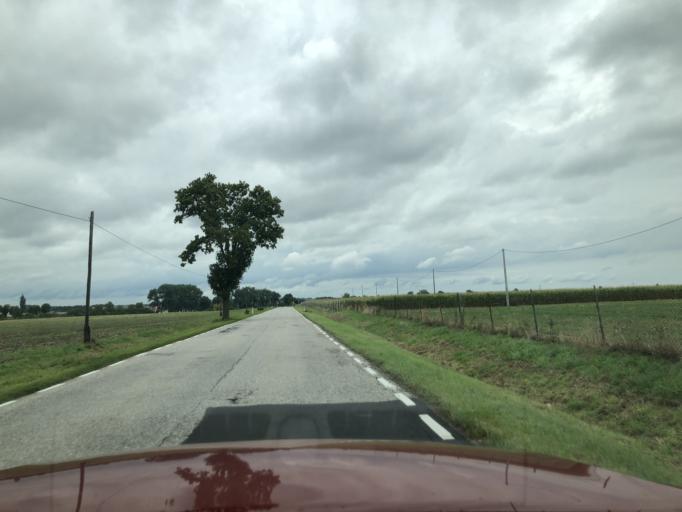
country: PL
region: Greater Poland Voivodeship
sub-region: Powiat szamotulski
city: Wronki
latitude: 52.6307
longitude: 16.3554
